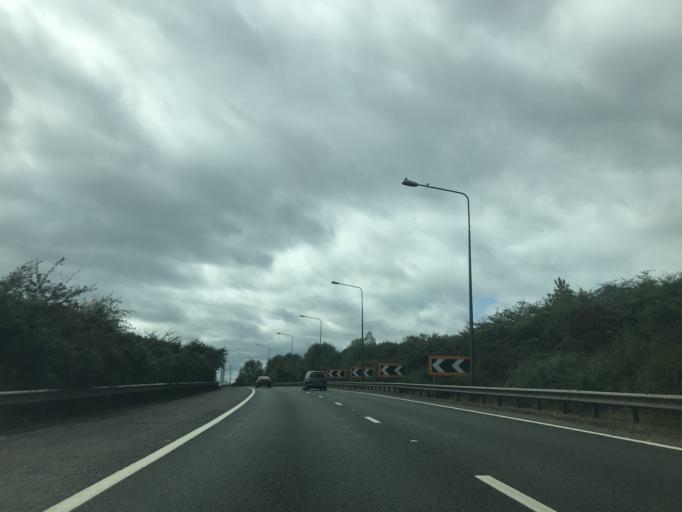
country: GB
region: England
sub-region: Buckinghamshire
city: Iver
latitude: 51.4935
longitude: -0.4907
